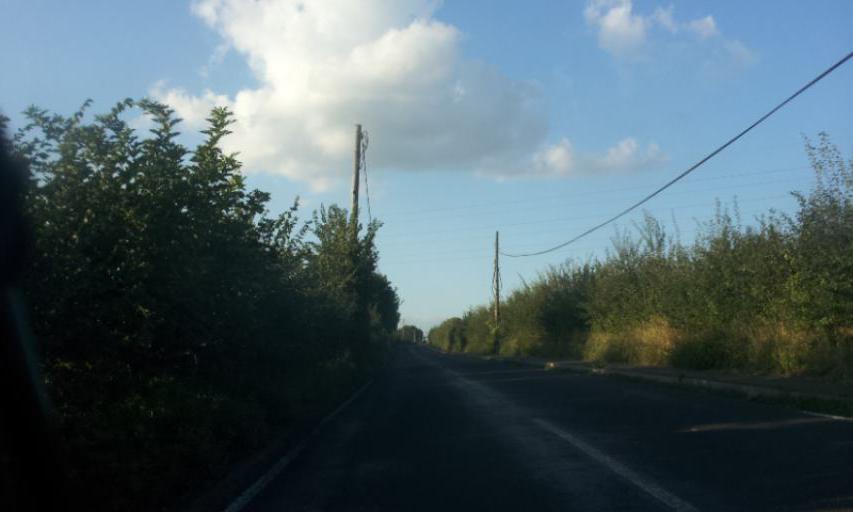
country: GB
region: England
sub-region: Medway
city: Halling
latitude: 51.3556
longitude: 0.4588
